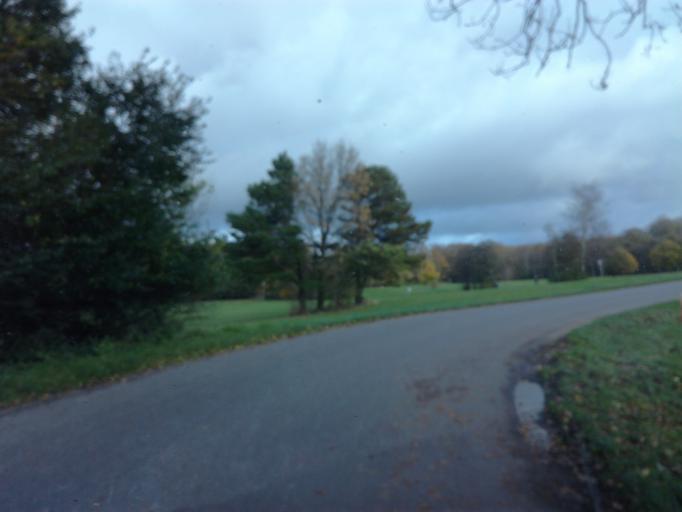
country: DK
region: South Denmark
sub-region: Vejle Kommune
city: Borkop
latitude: 55.6773
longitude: 9.5980
